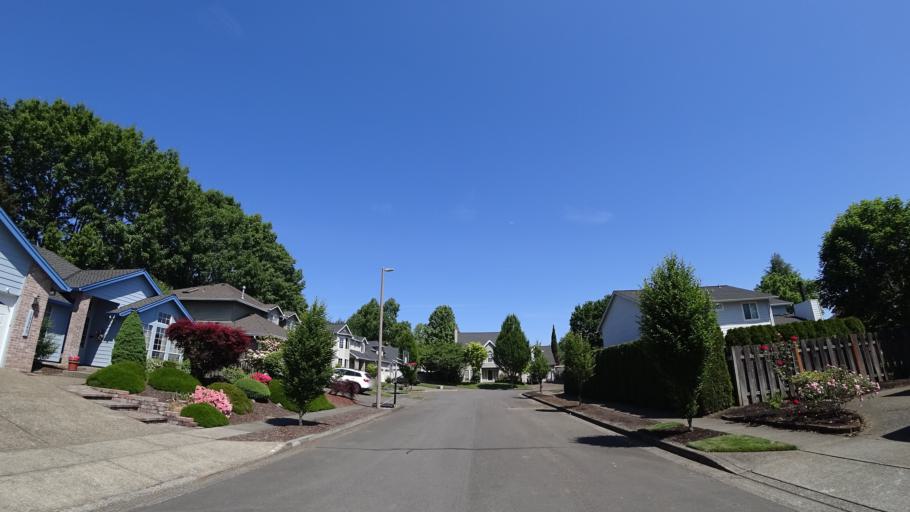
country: US
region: Oregon
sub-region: Washington County
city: Beaverton
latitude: 45.4452
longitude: -122.8143
